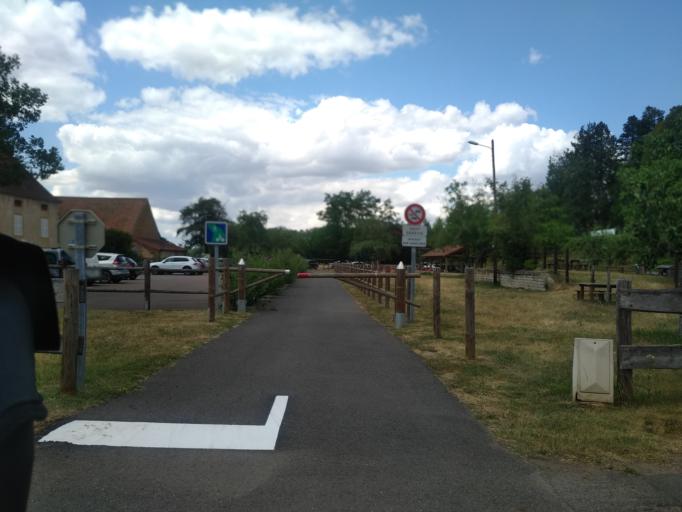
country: FR
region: Rhone-Alpes
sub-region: Departement de la Loire
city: Briennon
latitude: 46.2023
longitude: 4.0791
